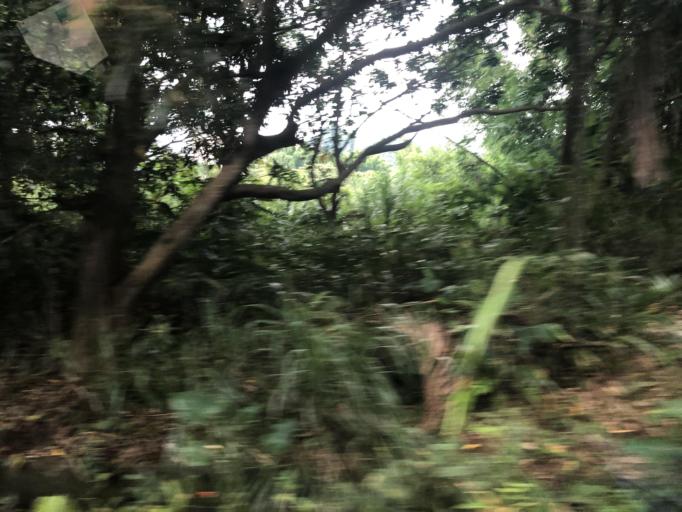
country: TW
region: Taiwan
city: Daxi
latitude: 24.9132
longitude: 121.3630
